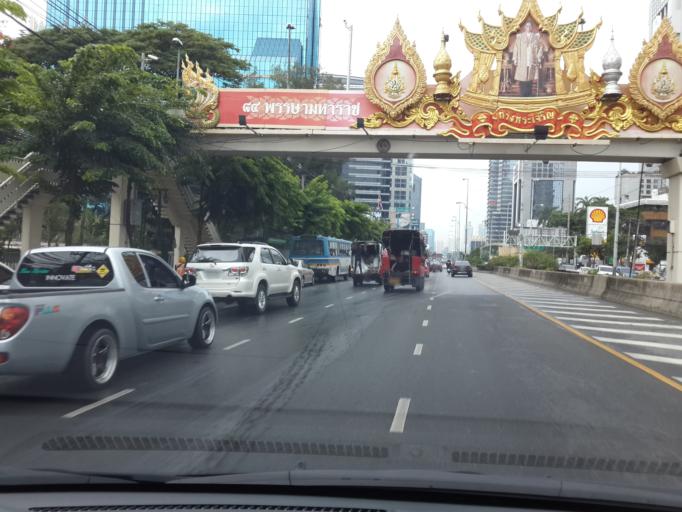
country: TH
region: Bangkok
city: Bang Rak
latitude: 13.7236
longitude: 100.5363
